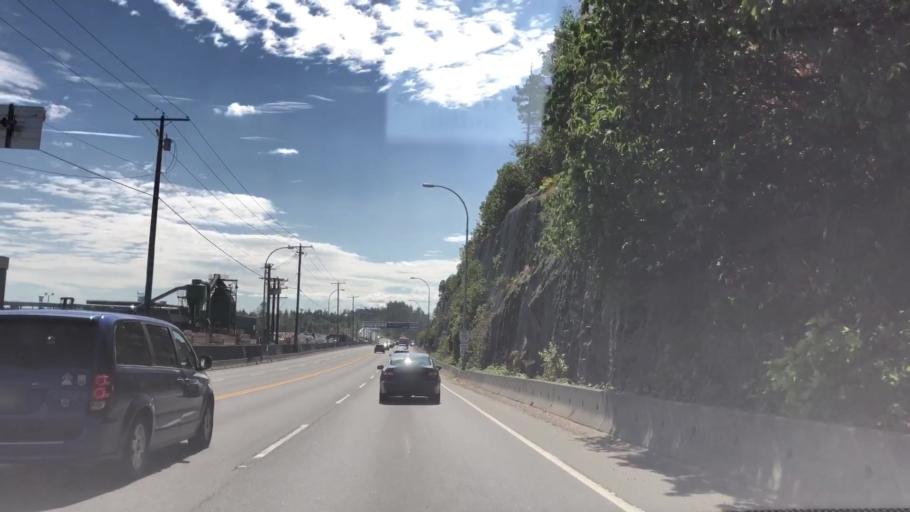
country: CA
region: British Columbia
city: Nanaimo
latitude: 49.1553
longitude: -123.8908
